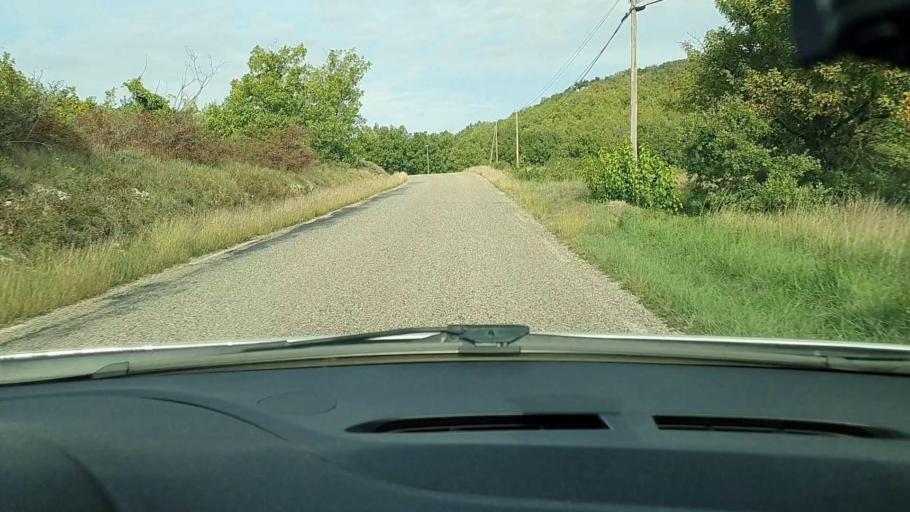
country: FR
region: Languedoc-Roussillon
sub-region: Departement du Gard
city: Goudargues
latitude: 44.1422
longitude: 4.3912
